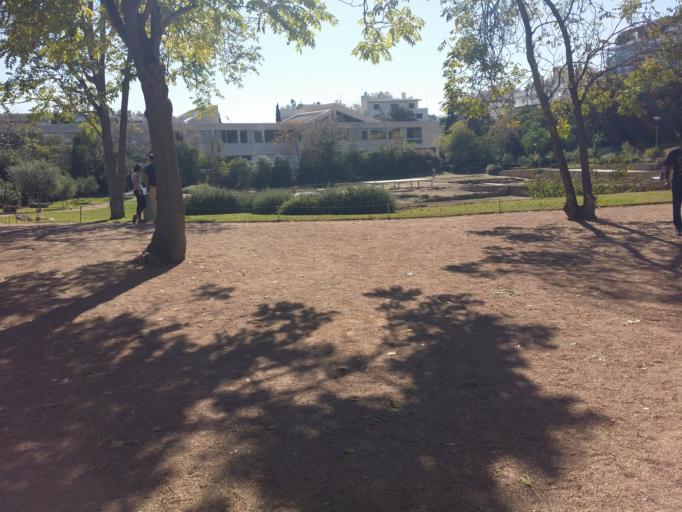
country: GR
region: Attica
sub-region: Nomarchia Athinas
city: Vyronas
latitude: 37.9746
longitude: 23.7437
